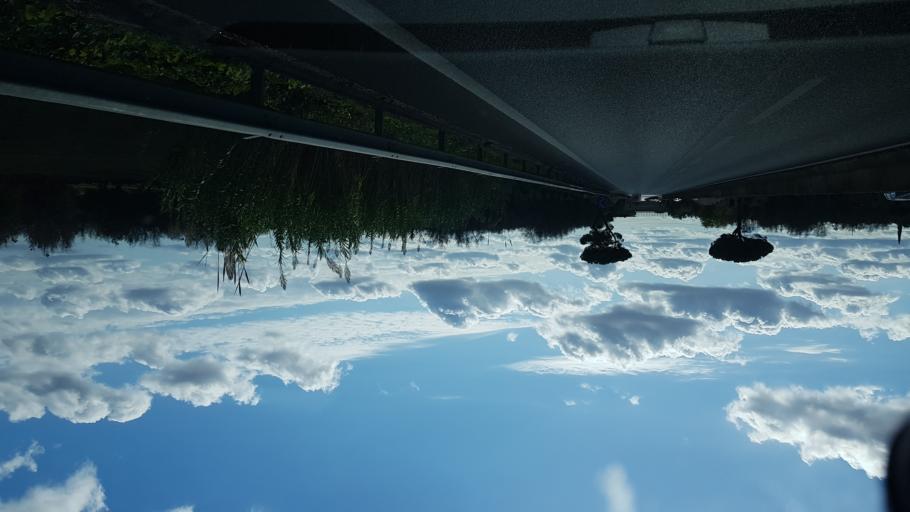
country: IT
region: Apulia
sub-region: Provincia di Brindisi
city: Torchiarolo
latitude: 40.4602
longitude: 18.0599
